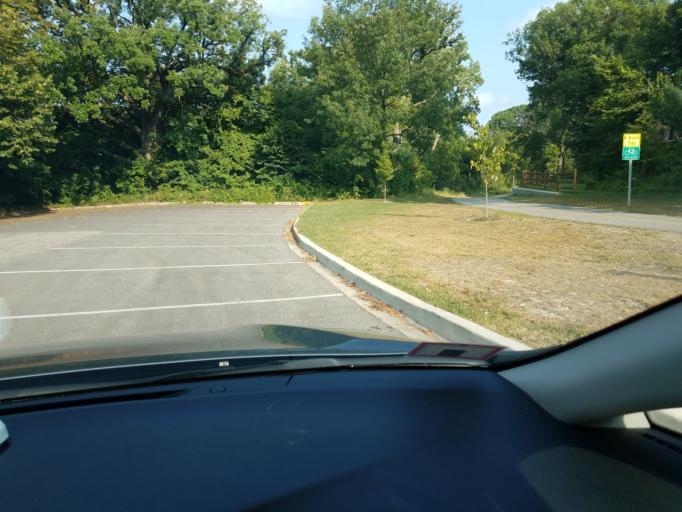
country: US
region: Illinois
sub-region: Cook County
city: Lincolnwood
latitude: 41.9813
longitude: -87.7563
